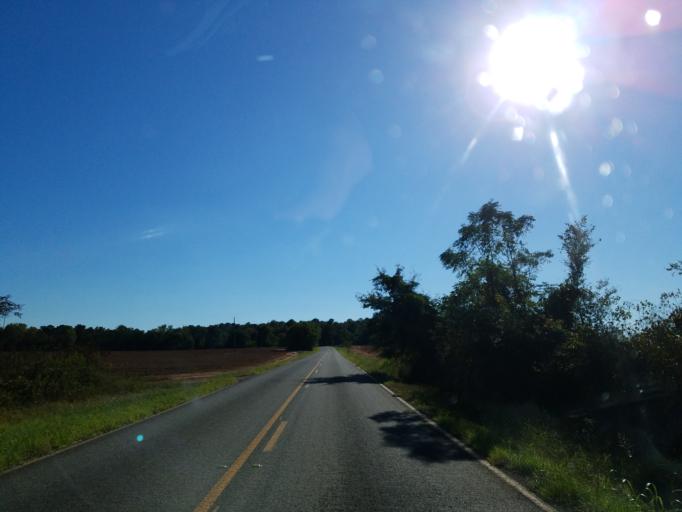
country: US
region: Georgia
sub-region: Dooly County
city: Unadilla
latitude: 32.2296
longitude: -83.8801
